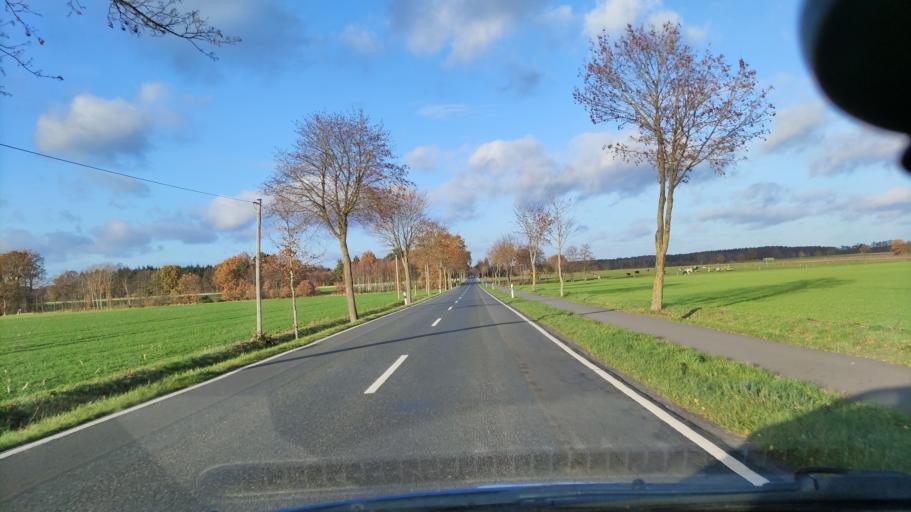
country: DE
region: Lower Saxony
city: Soltau
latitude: 53.0383
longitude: 9.8290
